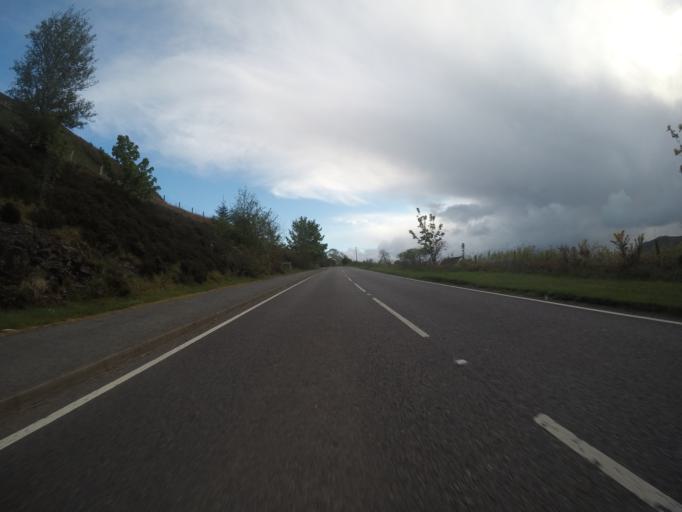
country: GB
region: Scotland
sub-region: Highland
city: Portree
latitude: 57.5883
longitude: -6.3554
